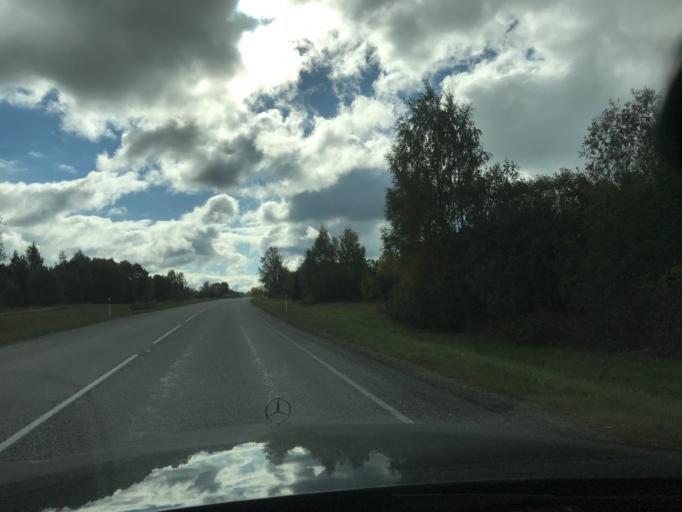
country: RU
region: Pskov
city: Pechory
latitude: 57.6944
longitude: 27.3275
